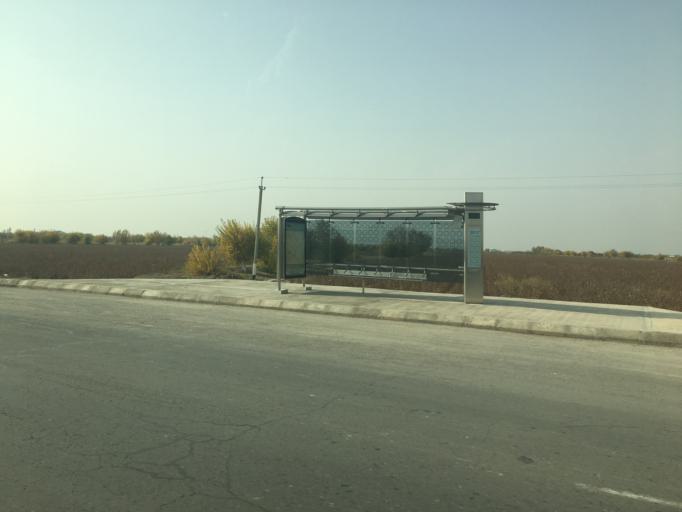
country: TM
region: Dasoguz
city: Dasoguz
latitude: 41.8059
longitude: 59.9046
